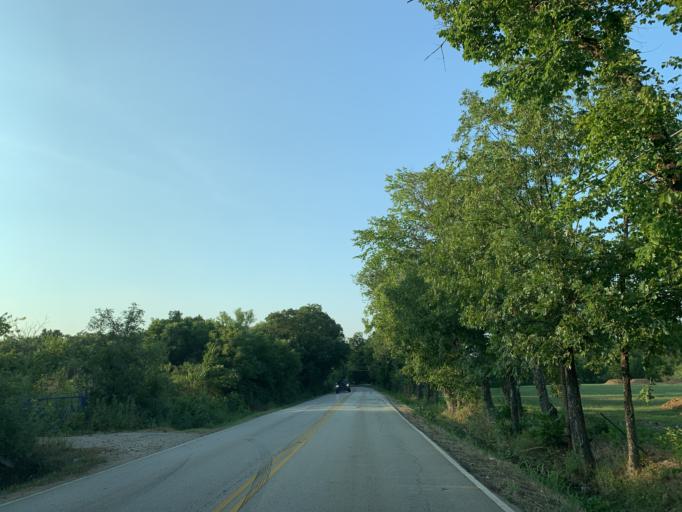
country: US
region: Texas
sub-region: Tarrant County
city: Hurst
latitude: 32.7766
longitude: -97.1749
